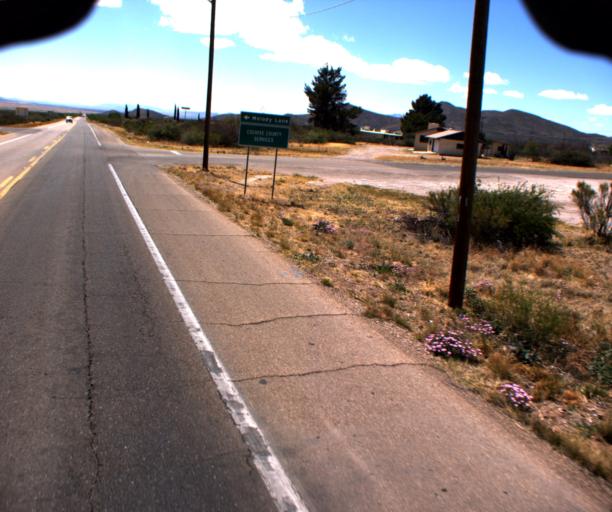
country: US
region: Arizona
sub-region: Cochise County
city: Bisbee
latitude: 31.3951
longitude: -109.9322
